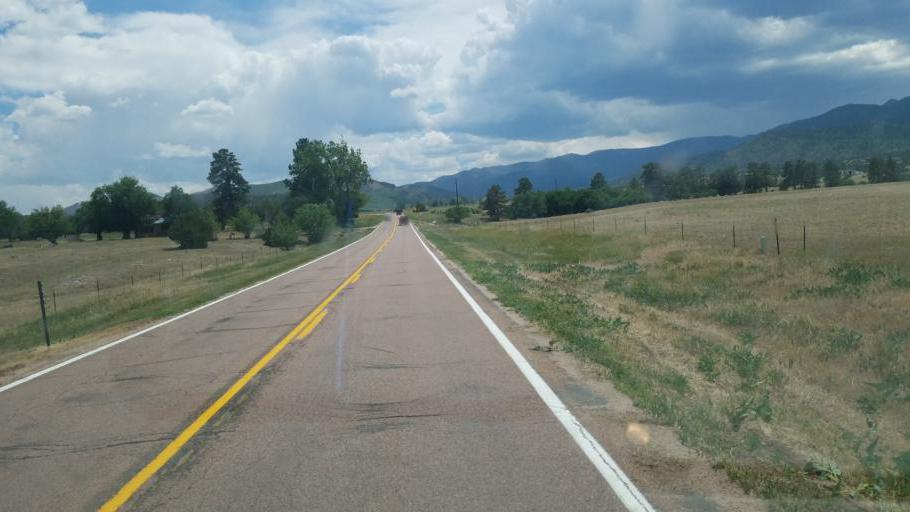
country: US
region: Colorado
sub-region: Fremont County
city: Florence
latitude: 38.2484
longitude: -105.0904
